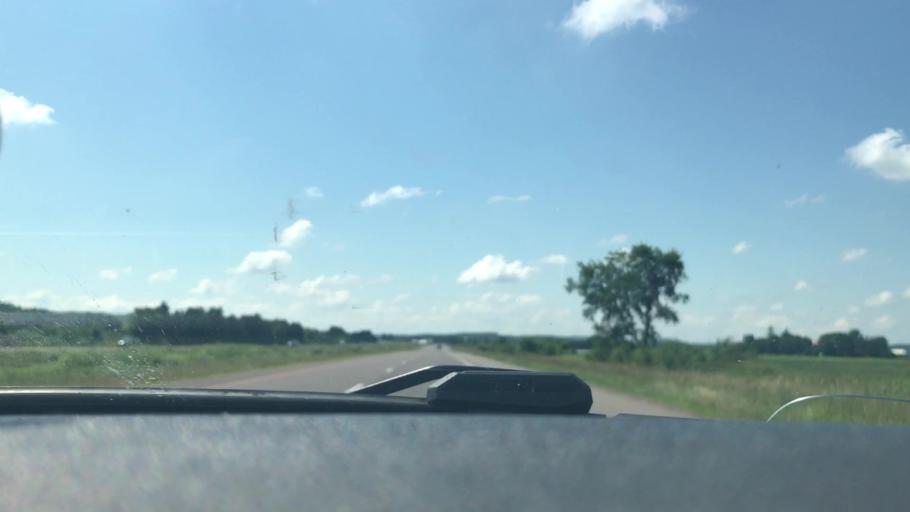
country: US
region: Wisconsin
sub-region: Chippewa County
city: Bloomer
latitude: 45.0613
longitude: -91.4659
